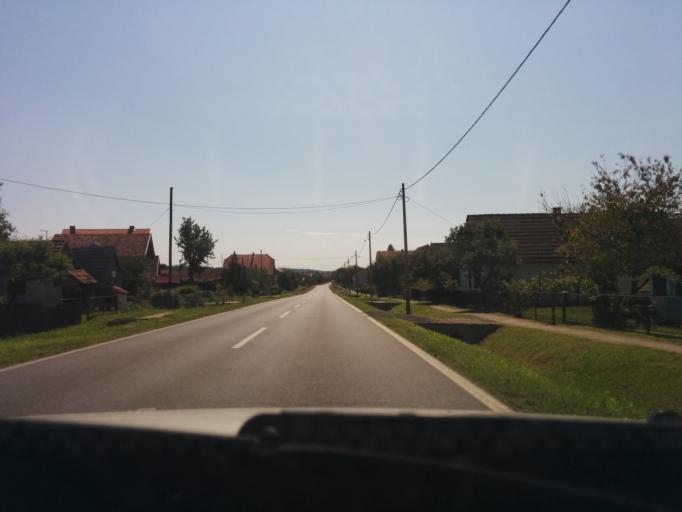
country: HR
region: Sisacko-Moslavacka
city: Lipovljani
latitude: 45.3707
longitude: 16.9238
